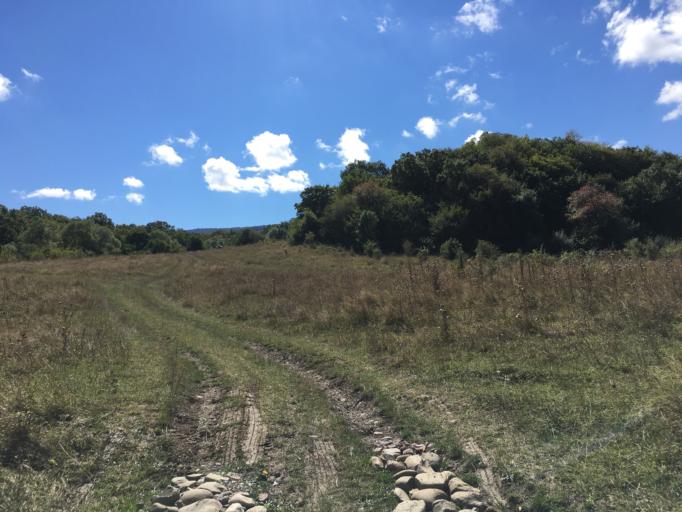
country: GE
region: Mtskheta-Mtianeti
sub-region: Tianetis Munitsip'alit'et'i
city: T'ianet'i
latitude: 41.9367
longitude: 44.9752
